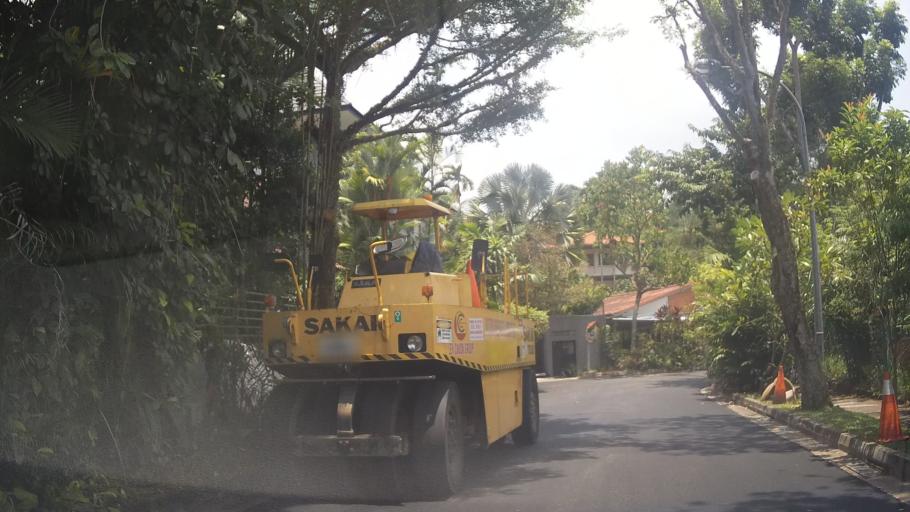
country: SG
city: Singapore
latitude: 1.3416
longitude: 103.7826
